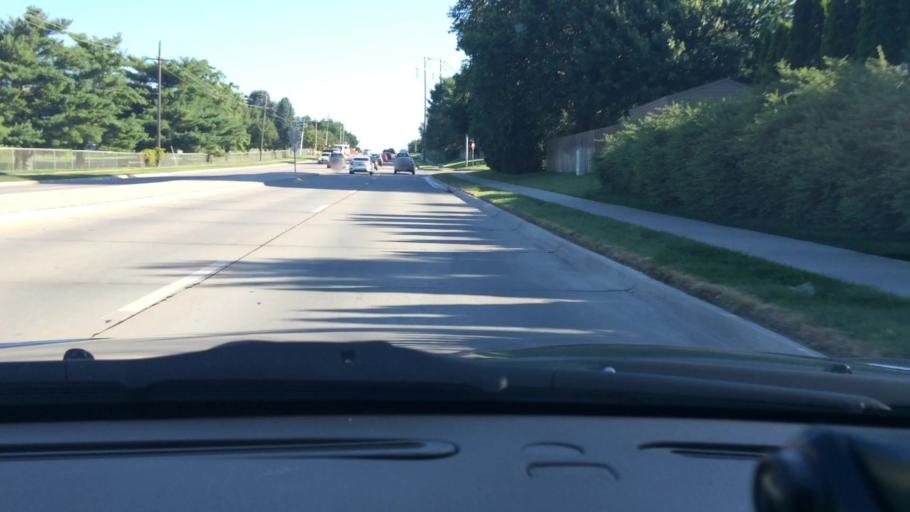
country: US
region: Nebraska
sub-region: Douglas County
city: Ralston
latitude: 41.1922
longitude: -96.0619
